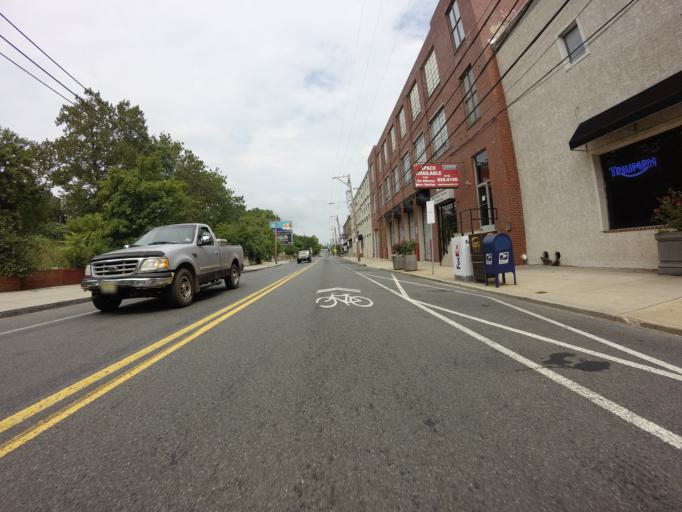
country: US
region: Pennsylvania
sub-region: Montgomery County
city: Bala-Cynwyd
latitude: 40.0201
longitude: -75.2156
